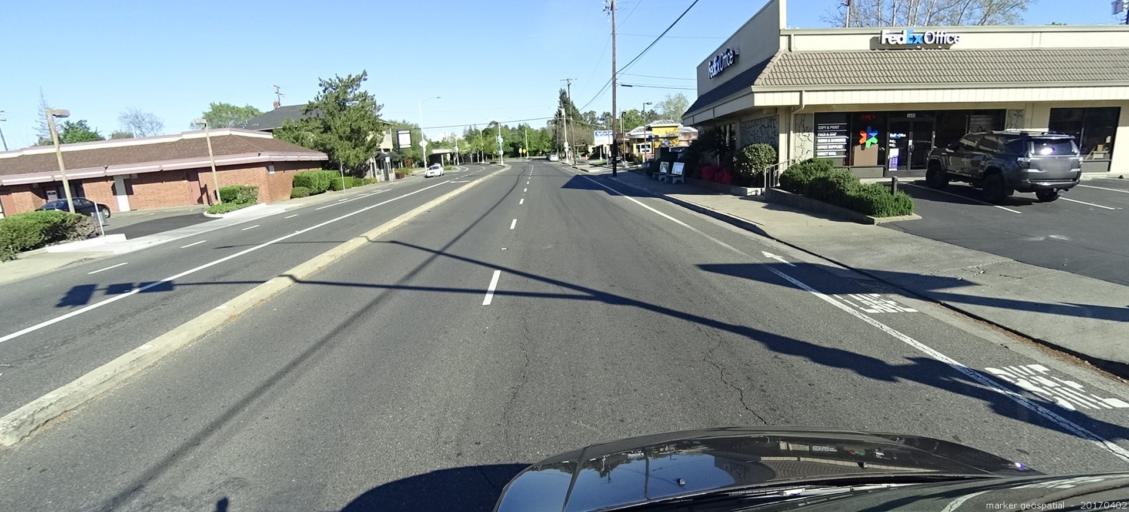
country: US
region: California
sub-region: Sacramento County
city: Sacramento
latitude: 38.5646
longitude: -121.4347
